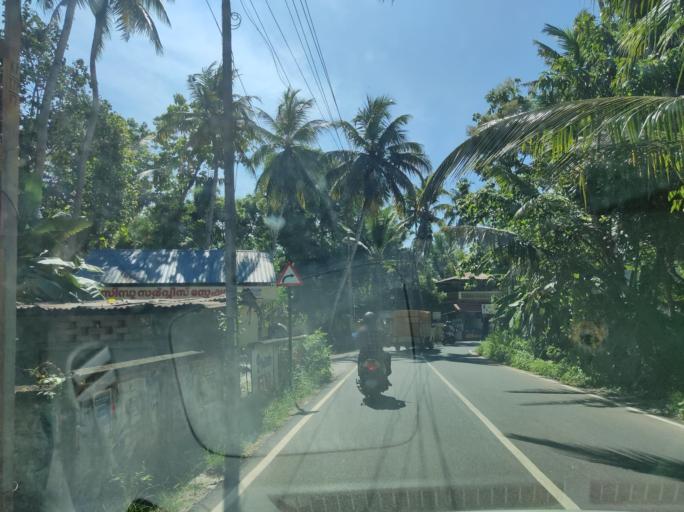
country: IN
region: Kerala
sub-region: Alappuzha
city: Kayankulam
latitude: 9.2610
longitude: 76.4086
